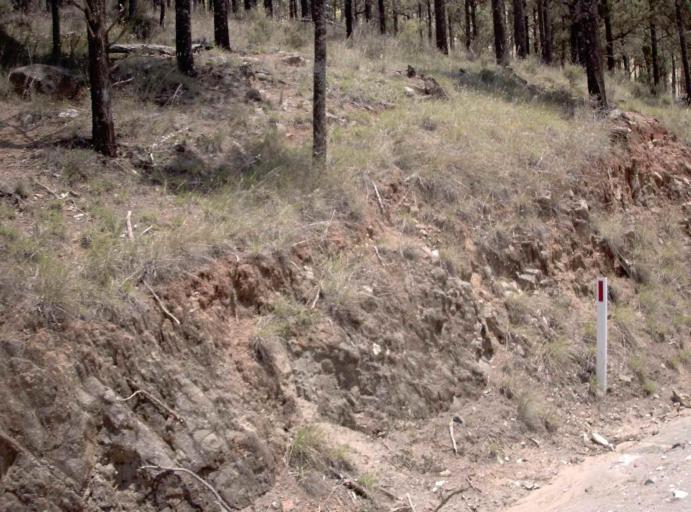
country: AU
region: New South Wales
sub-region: Snowy River
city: Jindabyne
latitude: -36.9071
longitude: 148.4158
